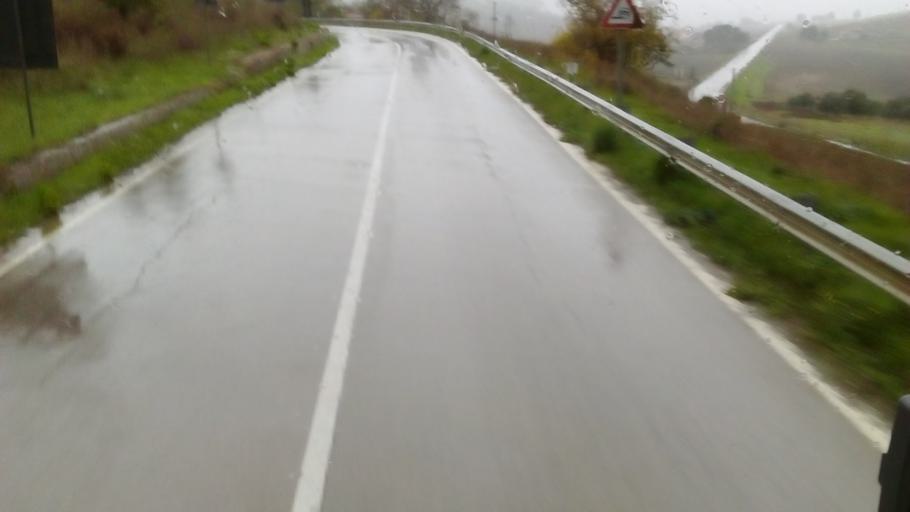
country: IT
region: Sicily
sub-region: Enna
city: Pietraperzia
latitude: 37.4279
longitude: 14.1674
